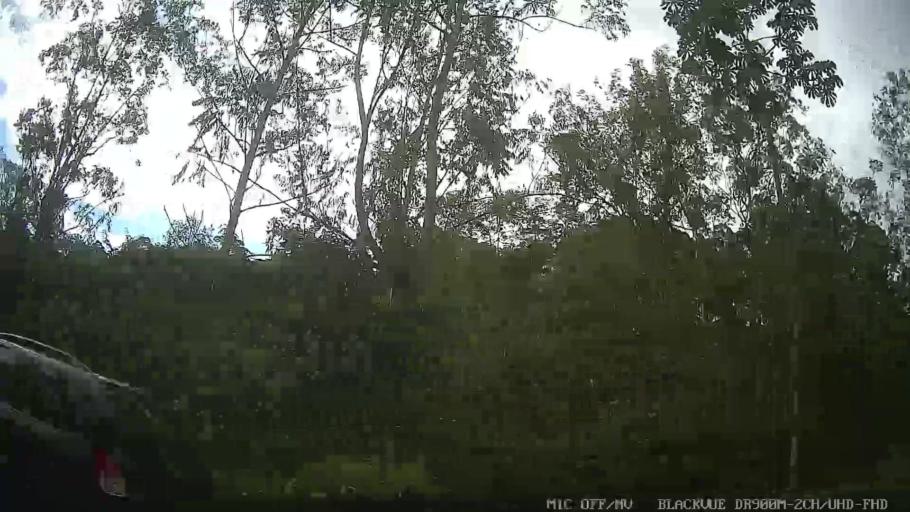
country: BR
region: Sao Paulo
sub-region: Santa Branca
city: Santa Branca
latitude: -23.5269
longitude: -45.7617
